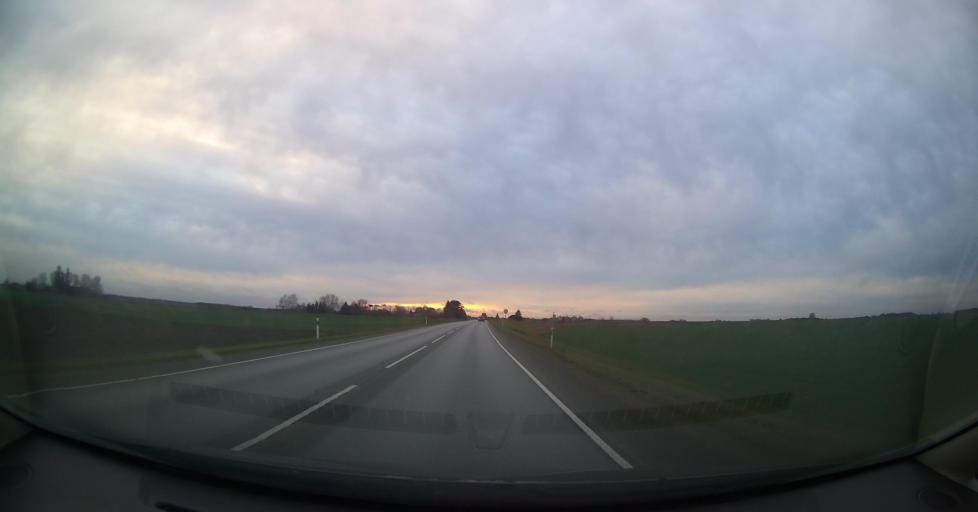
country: EE
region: Ida-Virumaa
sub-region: Kohtla-Nomme vald
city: Kohtla-Nomme
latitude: 59.4116
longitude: 27.1274
